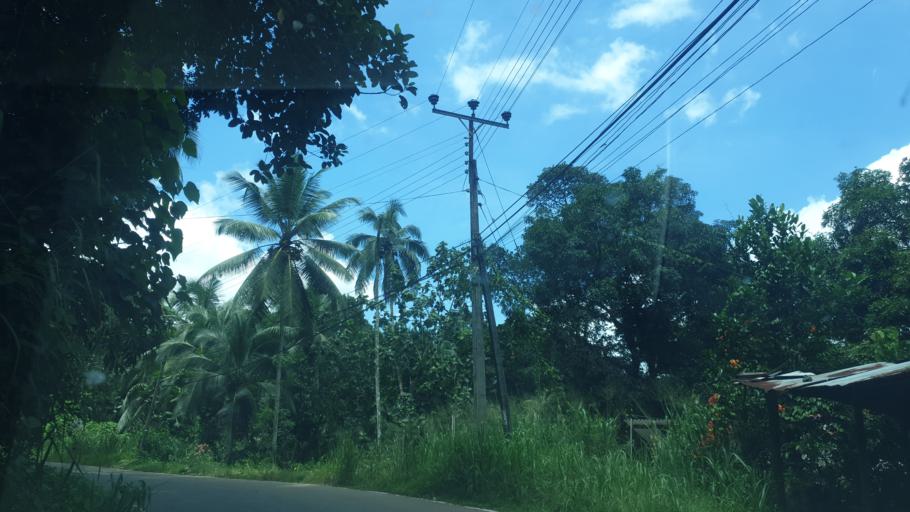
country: LK
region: Sabaragamuwa
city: Ratnapura
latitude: 6.4666
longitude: 80.4277
